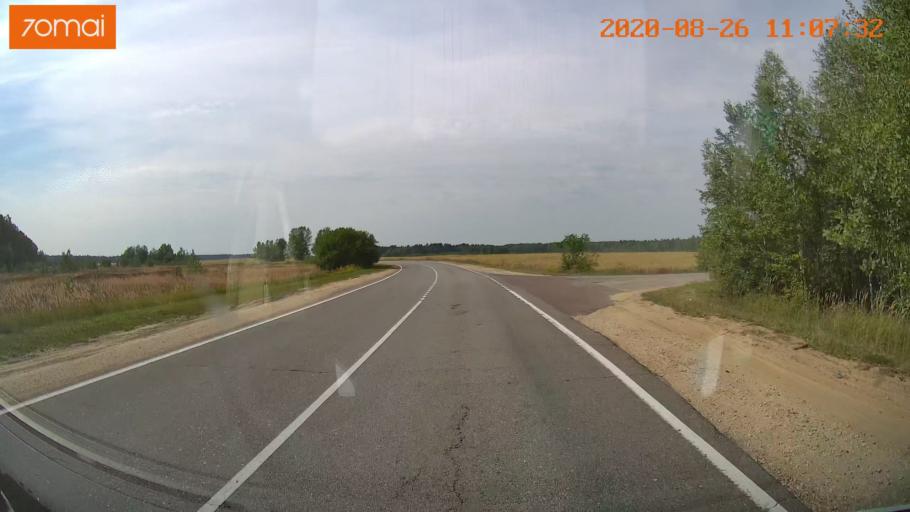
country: RU
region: Rjazan
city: Izhevskoye
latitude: 54.5172
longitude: 41.1225
